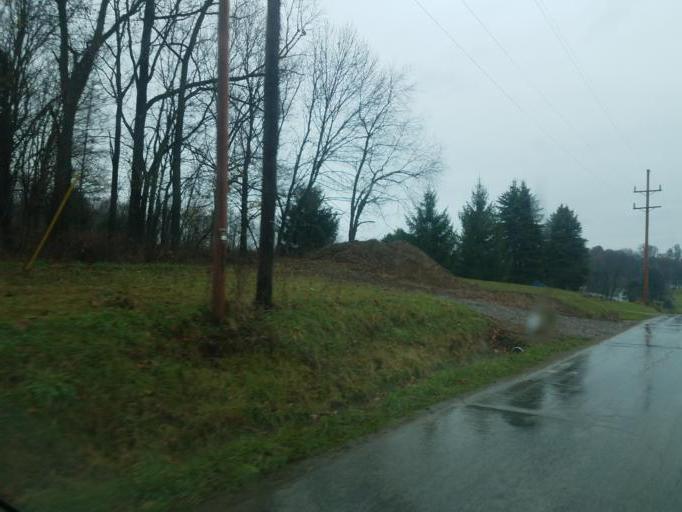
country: US
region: Ohio
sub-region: Sandusky County
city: Bellville
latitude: 40.5895
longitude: -82.5480
